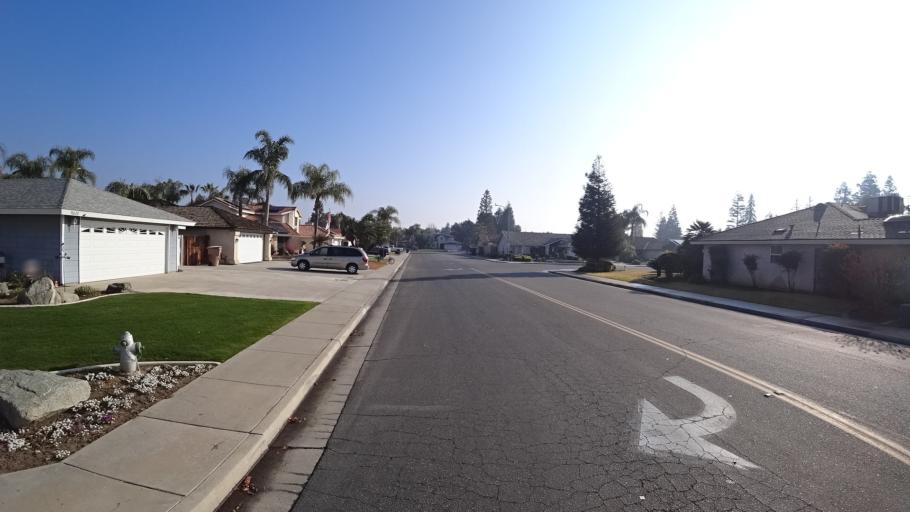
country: US
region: California
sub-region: Kern County
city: Greenacres
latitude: 35.3954
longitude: -119.1098
